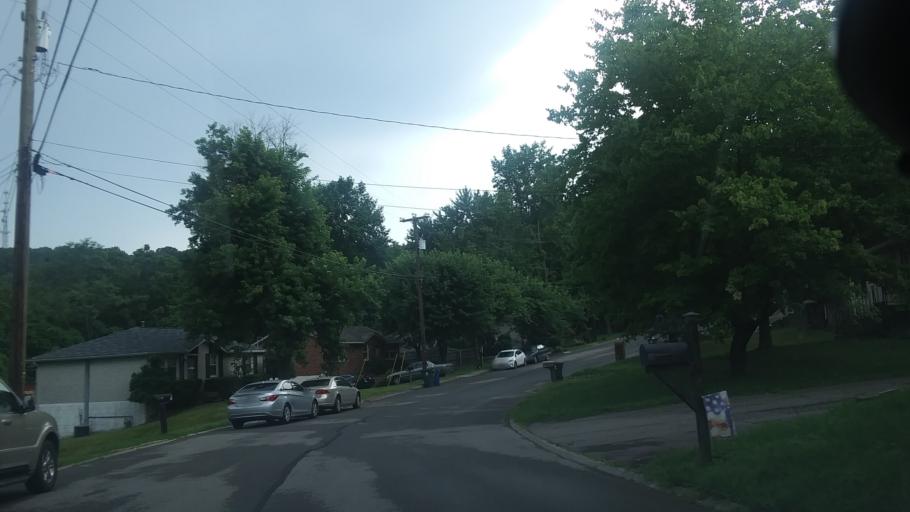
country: US
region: Tennessee
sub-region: Davidson County
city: Belle Meade
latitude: 36.0905
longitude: -86.9384
